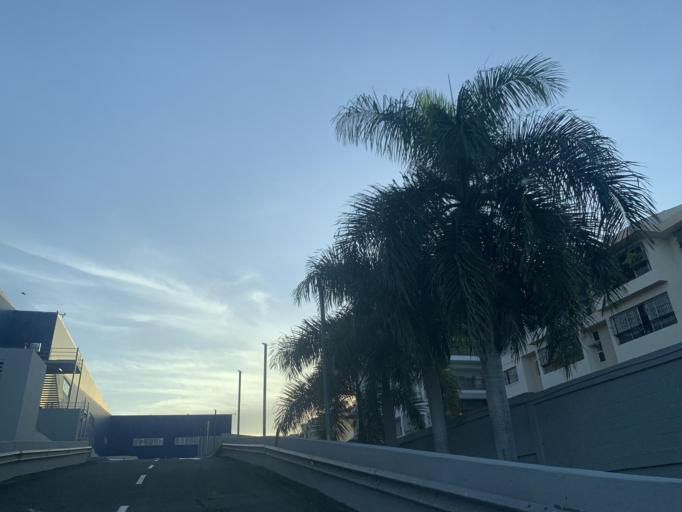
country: DO
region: Nacional
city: La Agustina
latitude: 18.4858
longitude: -69.9380
